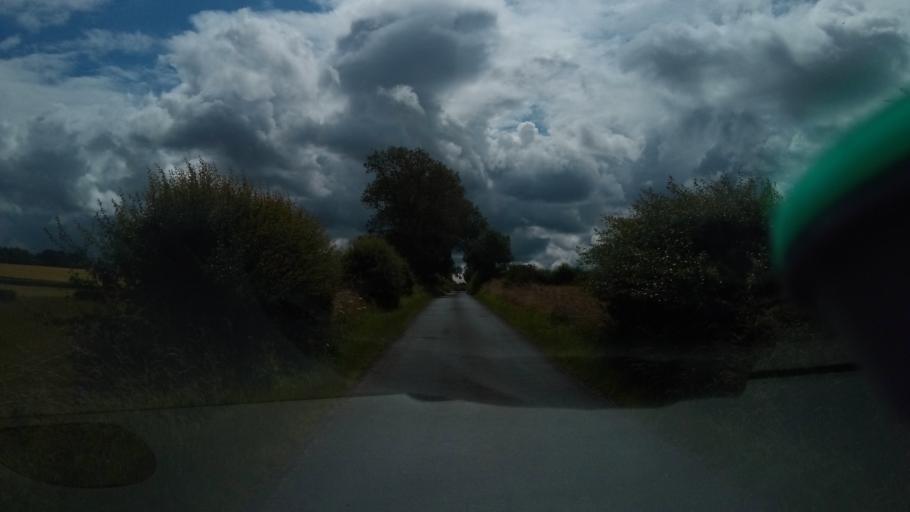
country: GB
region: Scotland
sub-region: The Scottish Borders
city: Kelso
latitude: 55.5104
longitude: -2.4199
